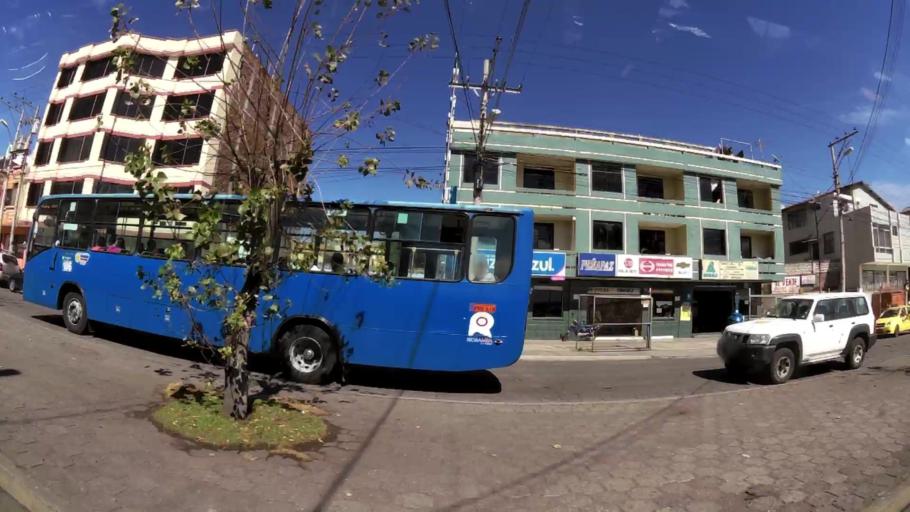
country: EC
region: Chimborazo
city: Riobamba
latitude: -1.6636
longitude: -78.6642
